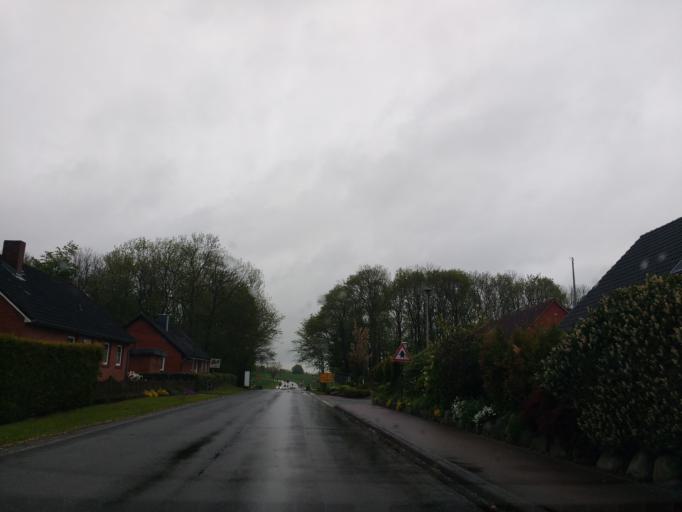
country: DE
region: Schleswig-Holstein
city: Damp
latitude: 54.5721
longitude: 9.9602
